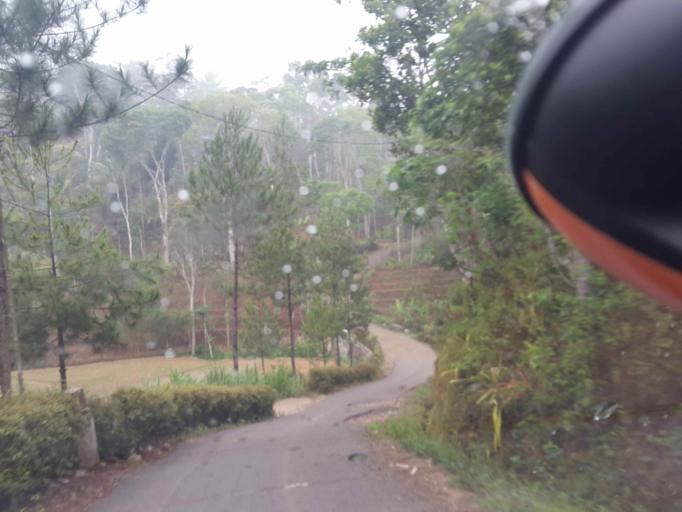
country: ID
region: East Java
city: Krajan Mrayan
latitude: -8.1078
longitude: 111.3415
